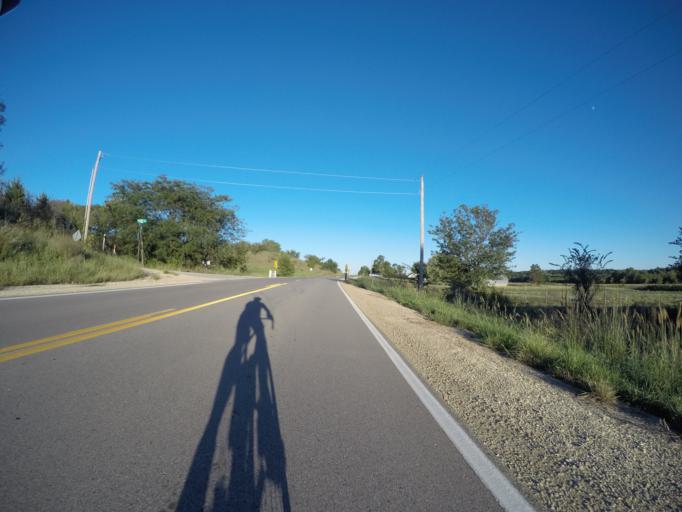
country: US
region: Kansas
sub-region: Riley County
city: Ogden
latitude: 39.2316
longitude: -96.7459
